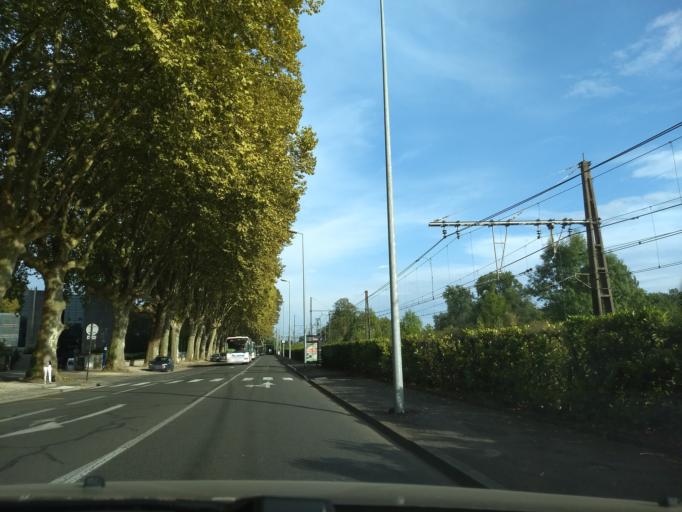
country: FR
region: Aquitaine
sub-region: Departement des Pyrenees-Atlantiques
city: Pau
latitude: 43.2934
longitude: -0.3758
